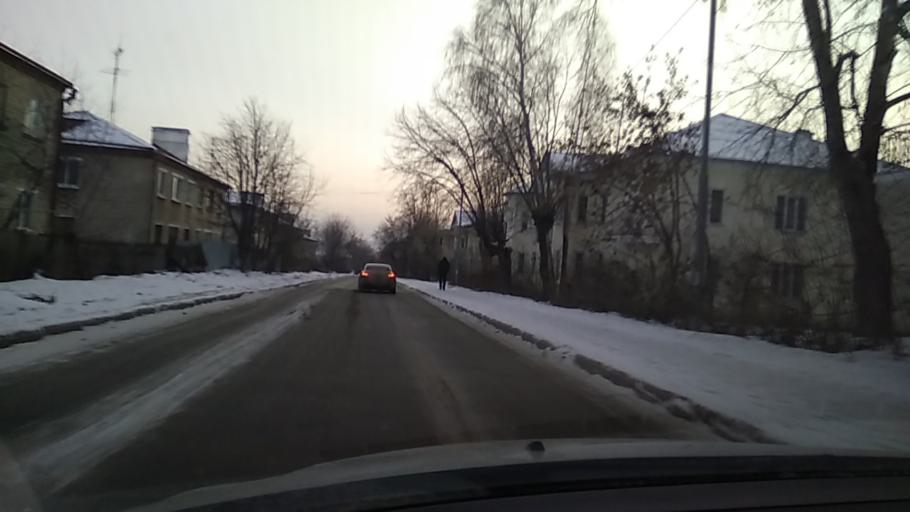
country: RU
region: Sverdlovsk
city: Istok
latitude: 56.7620
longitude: 60.7116
